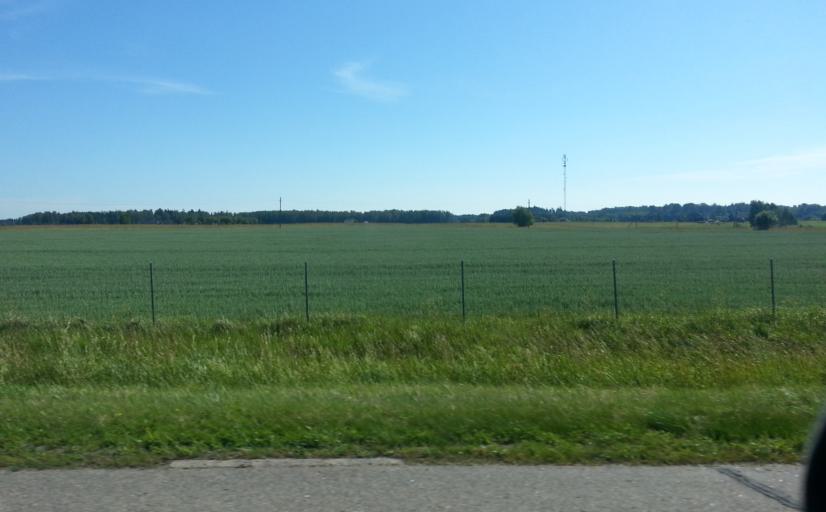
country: LT
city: Sirvintos
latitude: 55.0208
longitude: 24.9086
